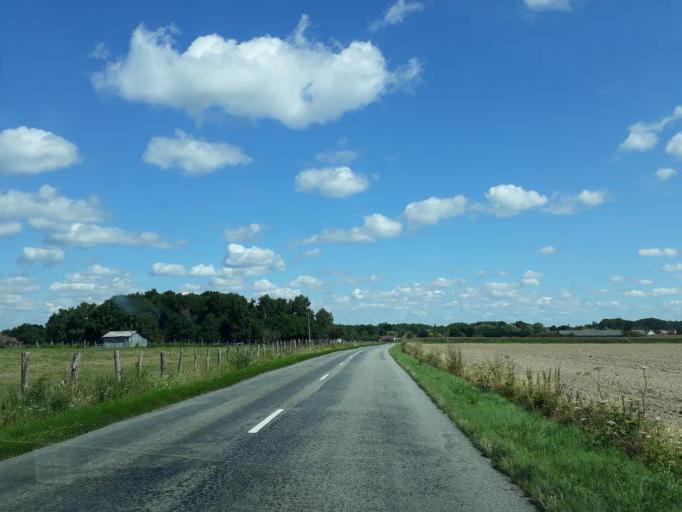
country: FR
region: Centre
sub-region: Departement du Loiret
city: Vitry-aux-Loges
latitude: 47.9235
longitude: 2.2571
